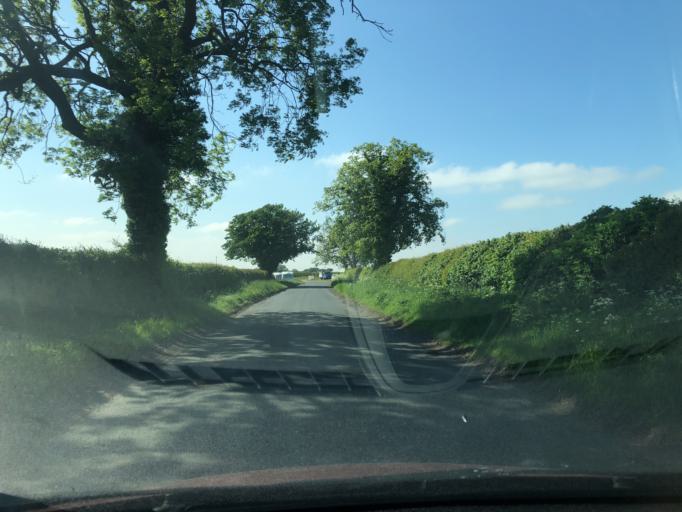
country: GB
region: England
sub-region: North Yorkshire
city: Northallerton
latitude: 54.3302
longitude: -1.4116
